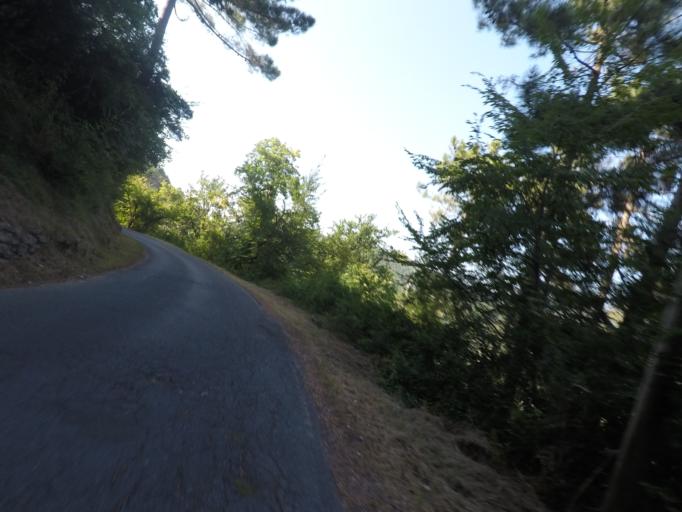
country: IT
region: Tuscany
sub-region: Provincia di Massa-Carrara
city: Carrara
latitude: 44.0799
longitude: 10.0663
